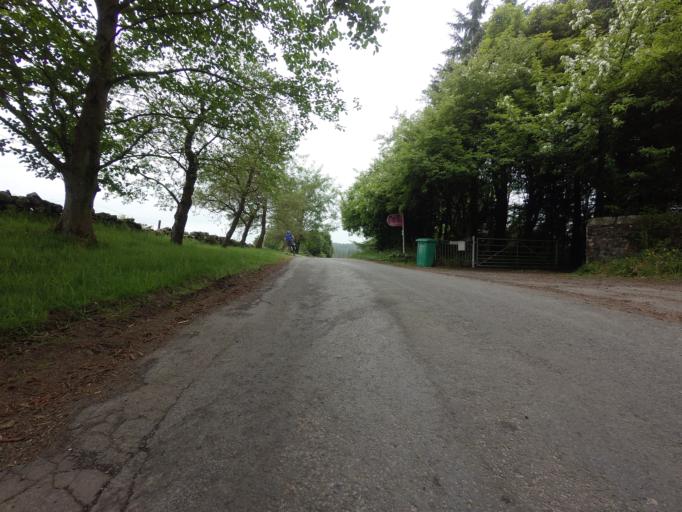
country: GB
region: Scotland
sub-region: Fife
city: Townhill
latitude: 56.1342
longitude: -3.4431
